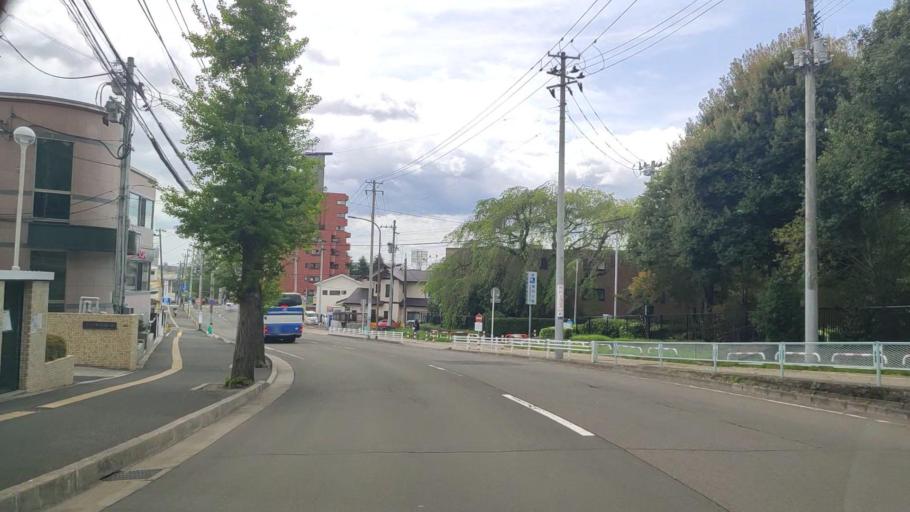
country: JP
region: Miyagi
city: Sendai-shi
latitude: 38.2600
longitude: 140.8993
